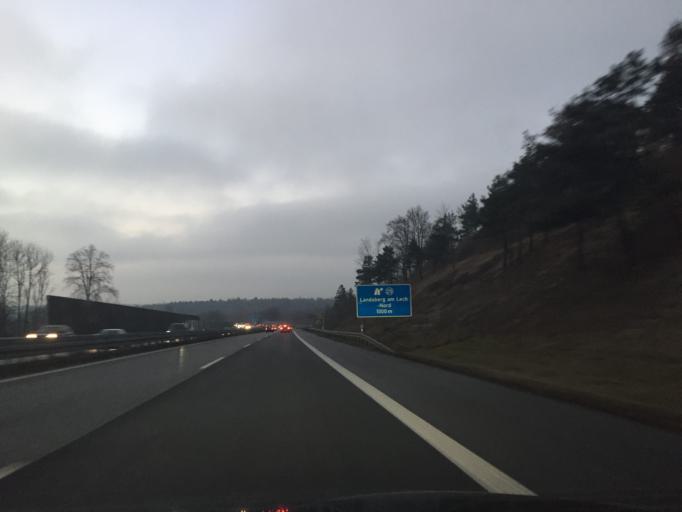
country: DE
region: Bavaria
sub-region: Upper Bavaria
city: Landsberg am Lech
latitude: 48.0618
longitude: 10.8806
